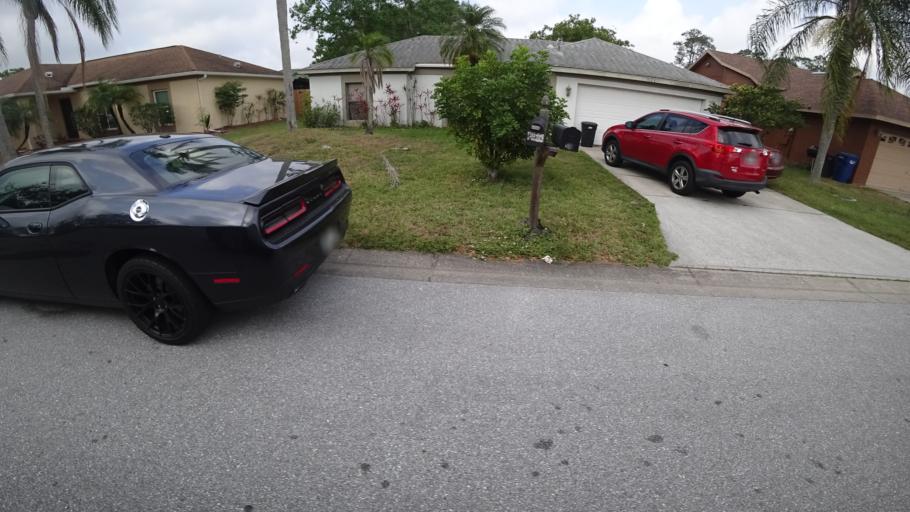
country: US
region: Florida
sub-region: Sarasota County
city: North Sarasota
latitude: 27.4046
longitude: -82.5158
